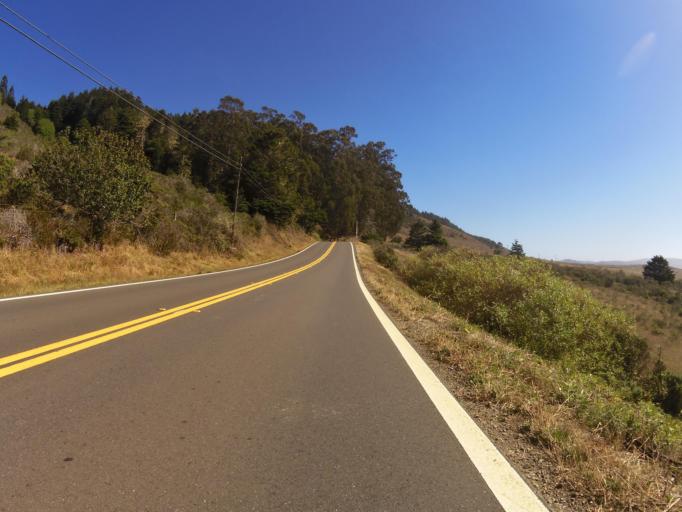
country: US
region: California
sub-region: Mendocino County
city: Fort Bragg
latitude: 39.5873
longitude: -123.7745
